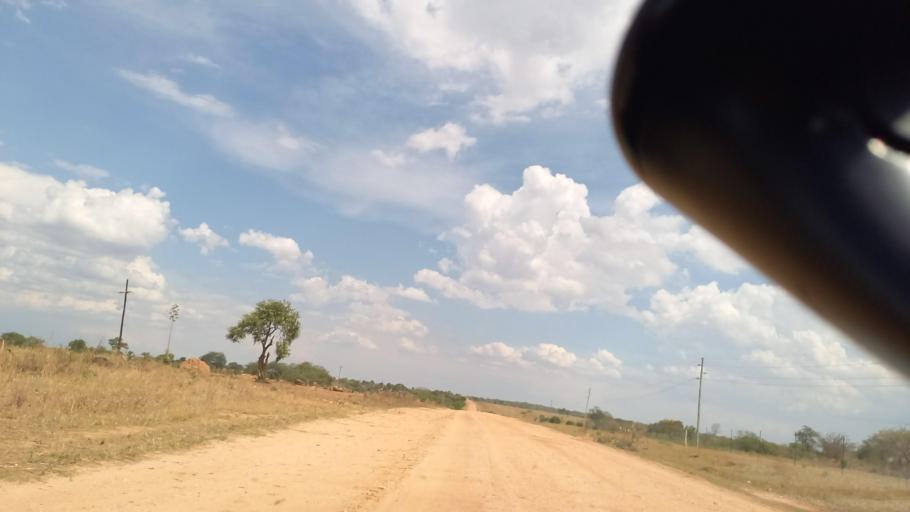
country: ZM
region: Southern
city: Nakambala
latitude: -16.1070
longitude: 28.0232
